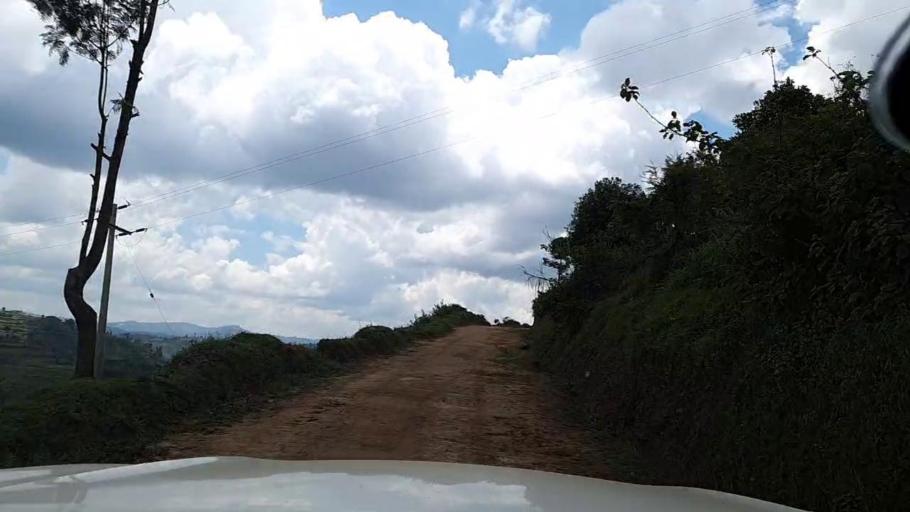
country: RW
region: Southern Province
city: Nzega
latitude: -2.6367
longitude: 29.4885
